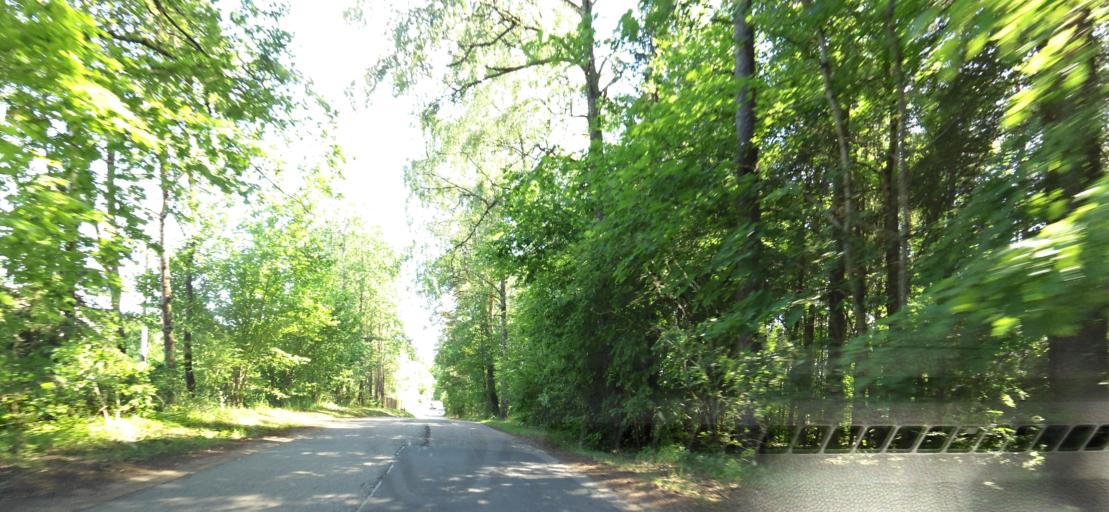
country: LT
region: Vilnius County
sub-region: Vilnius
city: Fabijoniskes
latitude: 54.8163
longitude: 25.3215
